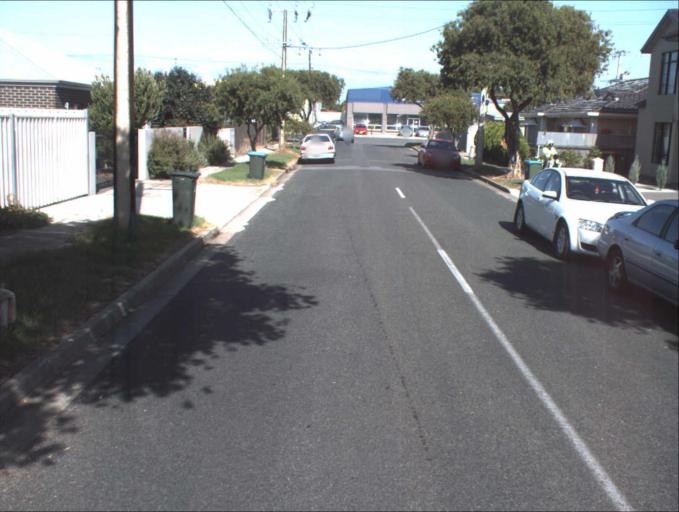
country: AU
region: South Australia
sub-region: Prospect
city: Prospect
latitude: -34.8770
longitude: 138.5724
